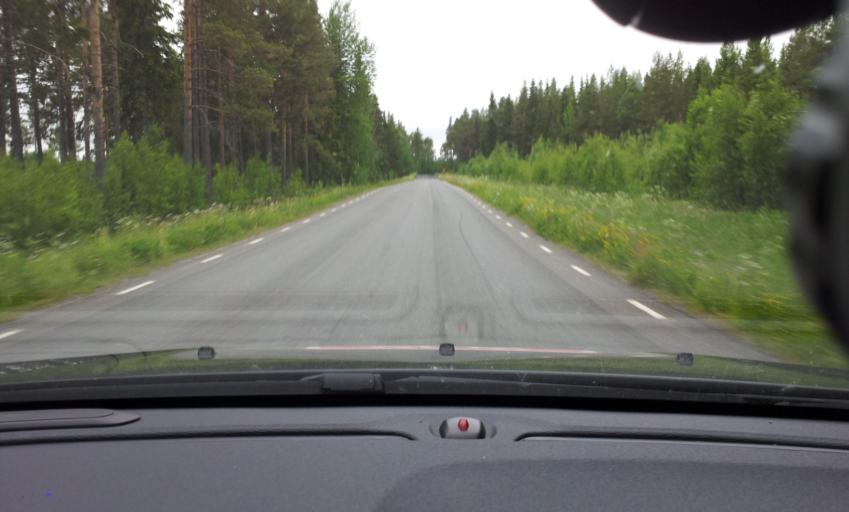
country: SE
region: Jaemtland
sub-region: Krokoms Kommun
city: Valla
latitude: 63.2860
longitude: 13.7755
